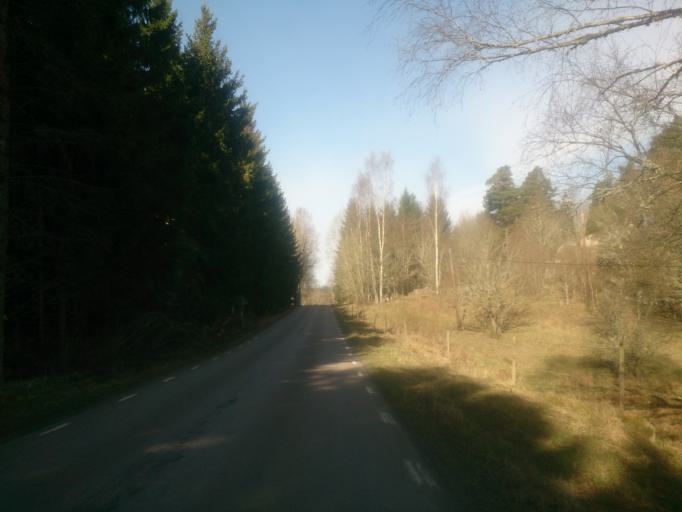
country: SE
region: OEstergoetland
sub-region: Linkopings Kommun
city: Sturefors
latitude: 58.2979
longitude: 15.8391
